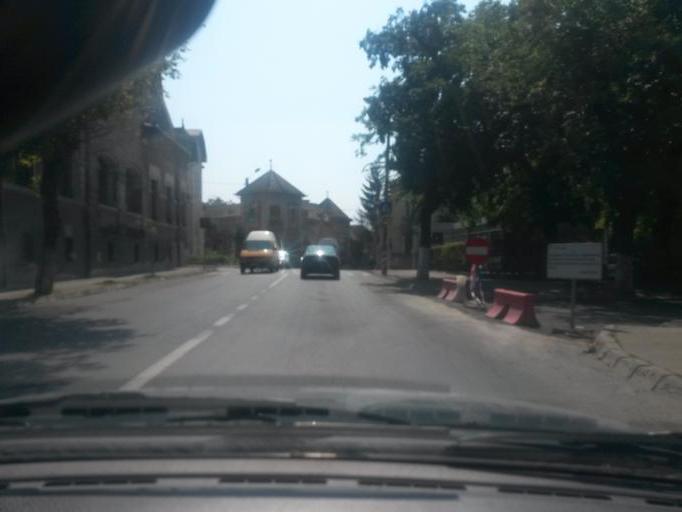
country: RO
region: Mures
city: Targu-Mures
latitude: 46.5484
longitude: 24.5724
